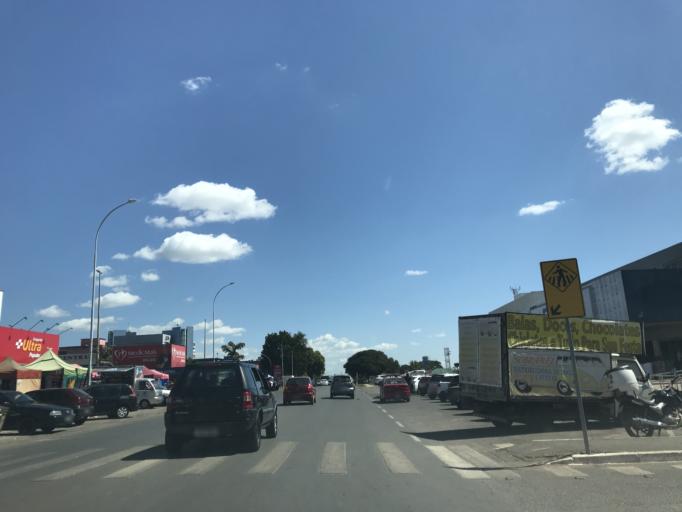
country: BR
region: Federal District
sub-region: Brasilia
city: Brasilia
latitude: -15.6501
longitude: -47.7905
